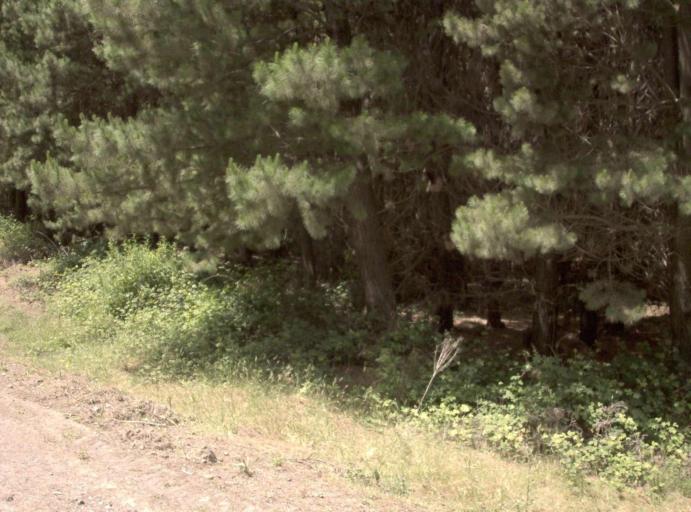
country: AU
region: Victoria
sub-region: Latrobe
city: Traralgon
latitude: -38.3823
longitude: 146.6660
